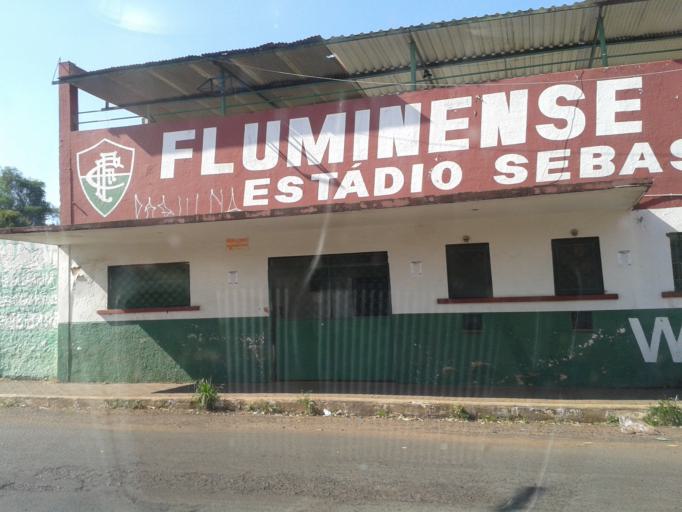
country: BR
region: Minas Gerais
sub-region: Araguari
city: Araguari
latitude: -18.6529
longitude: -48.1826
